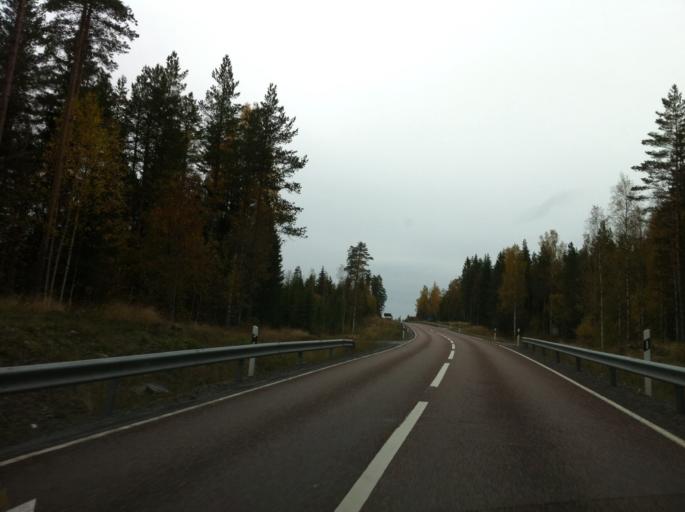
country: SE
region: Dalarna
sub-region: Ludvika Kommun
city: Grangesberg
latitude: 60.0431
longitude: 14.9756
